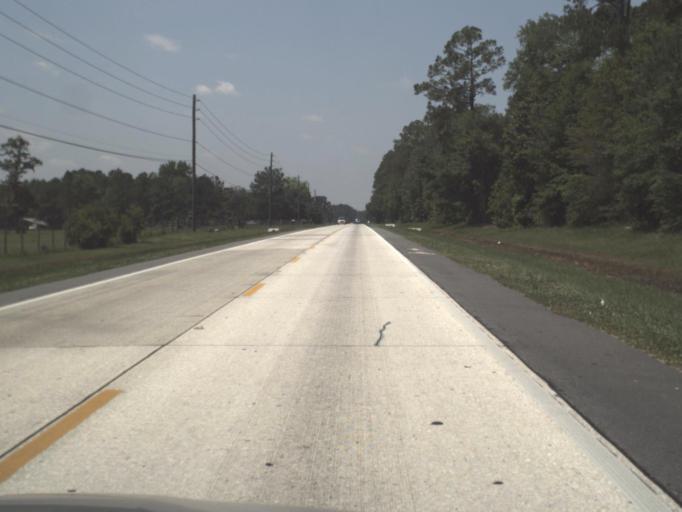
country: US
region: Florida
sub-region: Duval County
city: Baldwin
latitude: 30.2275
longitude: -81.9241
